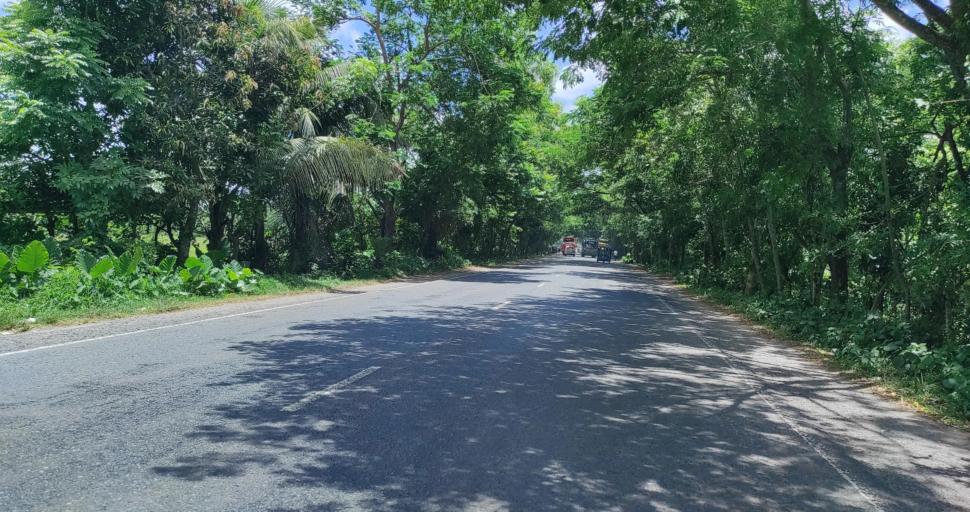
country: BD
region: Barisal
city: Gaurnadi
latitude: 22.8334
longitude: 90.2549
